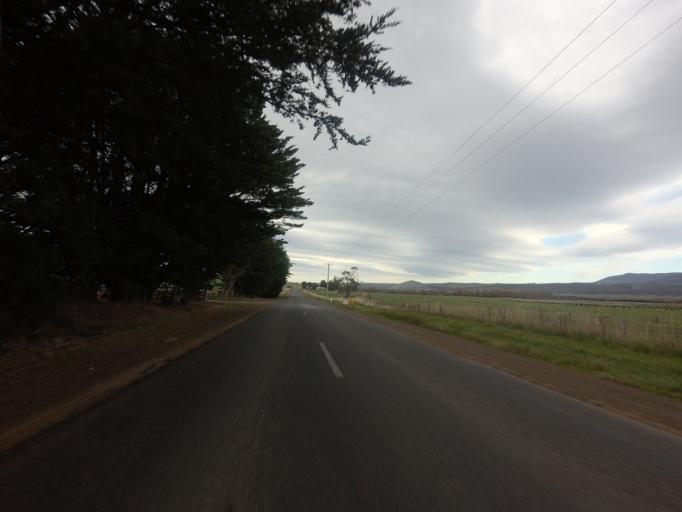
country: AU
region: Tasmania
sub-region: Derwent Valley
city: New Norfolk
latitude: -42.4992
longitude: 146.7322
